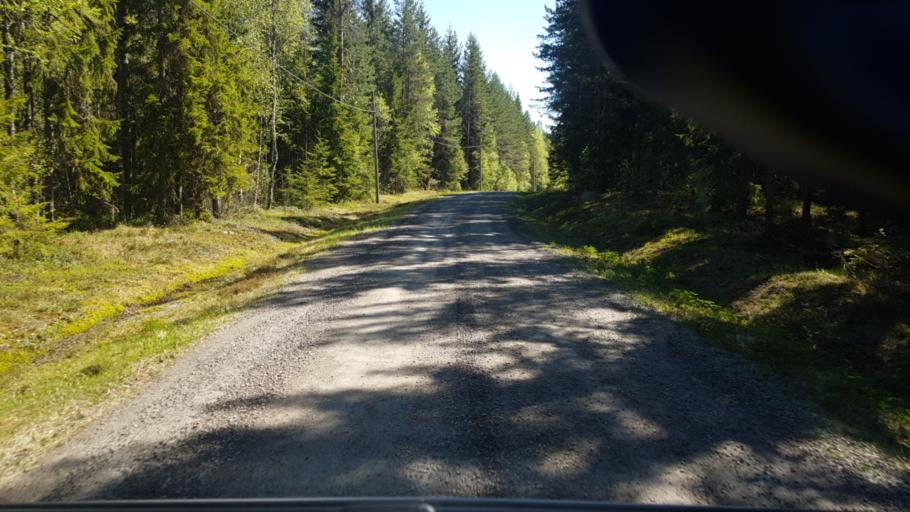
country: SE
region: Vaermland
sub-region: Eda Kommun
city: Charlottenberg
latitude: 59.9064
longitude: 12.3810
